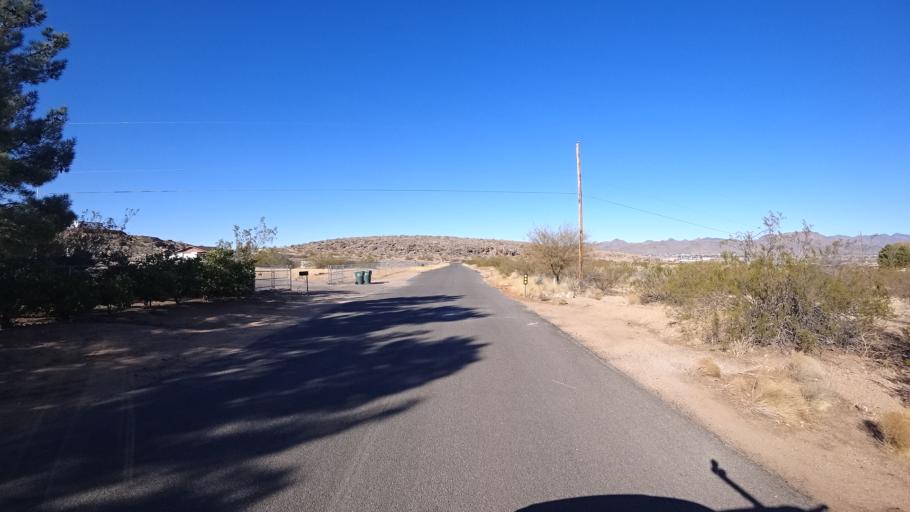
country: US
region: Arizona
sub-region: Mohave County
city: Kingman
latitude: 35.2066
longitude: -114.0001
